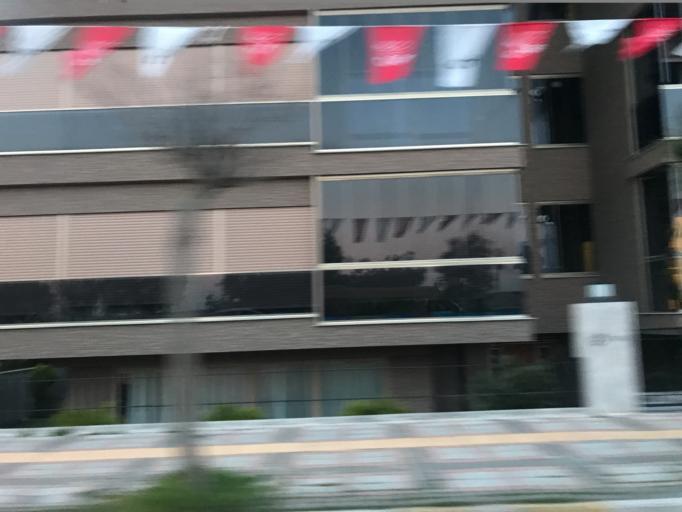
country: TR
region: Istanbul
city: Bahcelievler
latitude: 40.9619
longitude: 28.8408
